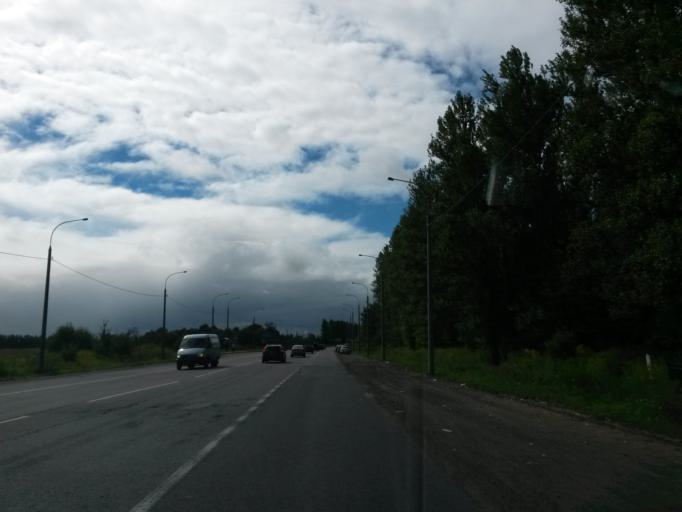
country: RU
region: Jaroslavl
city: Yaroslavl
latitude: 57.6545
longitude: 39.7531
